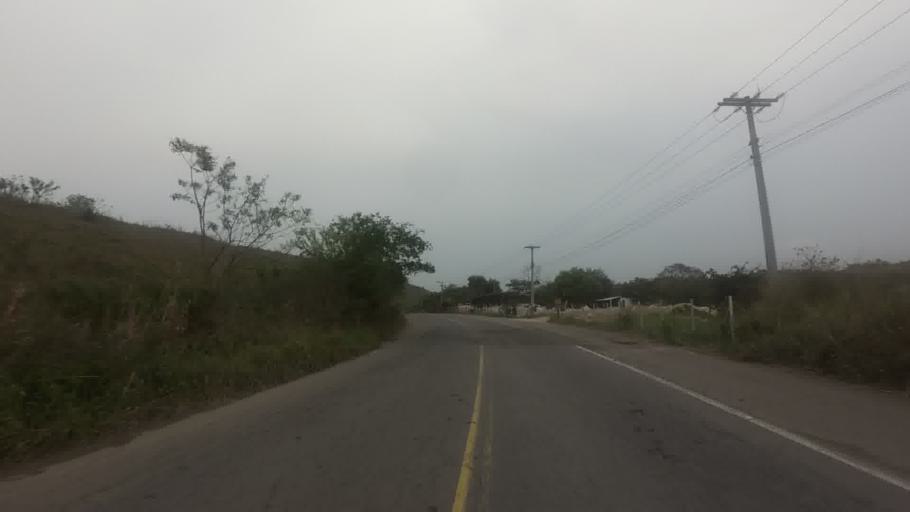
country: BR
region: Rio de Janeiro
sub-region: Santo Antonio De Padua
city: Santo Antonio de Padua
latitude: -21.6012
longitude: -42.2360
